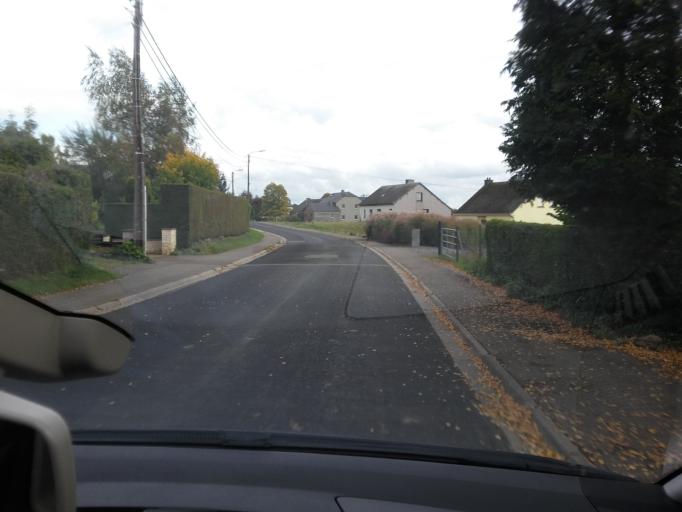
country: BE
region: Wallonia
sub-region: Province du Luxembourg
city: Attert
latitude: 49.7001
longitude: 5.7543
